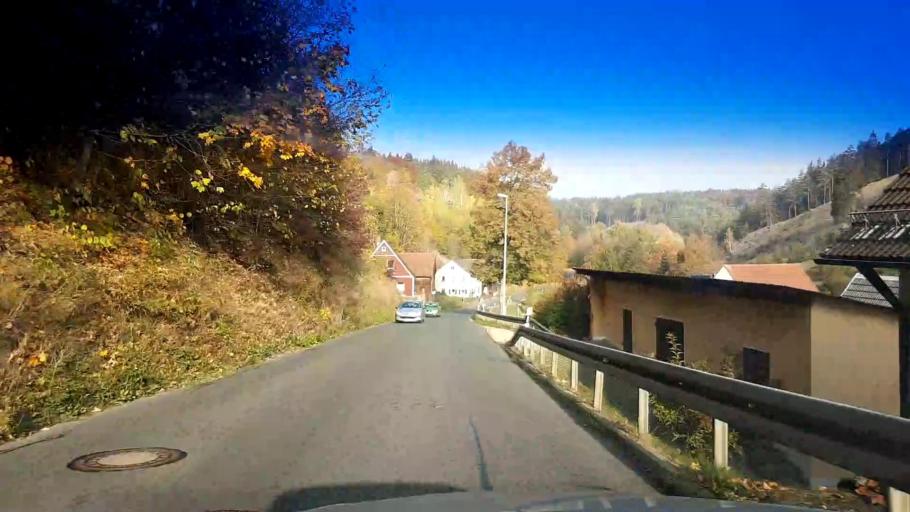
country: DE
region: Bavaria
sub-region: Upper Franconia
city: Stadelhofen
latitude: 50.0211
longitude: 11.2000
